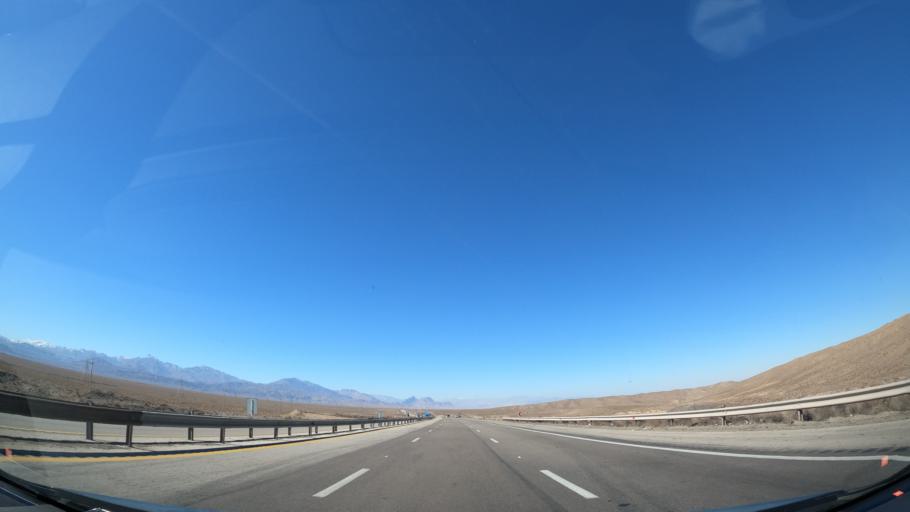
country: IR
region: Isfahan
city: Kashan
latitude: 33.8274
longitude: 51.6211
